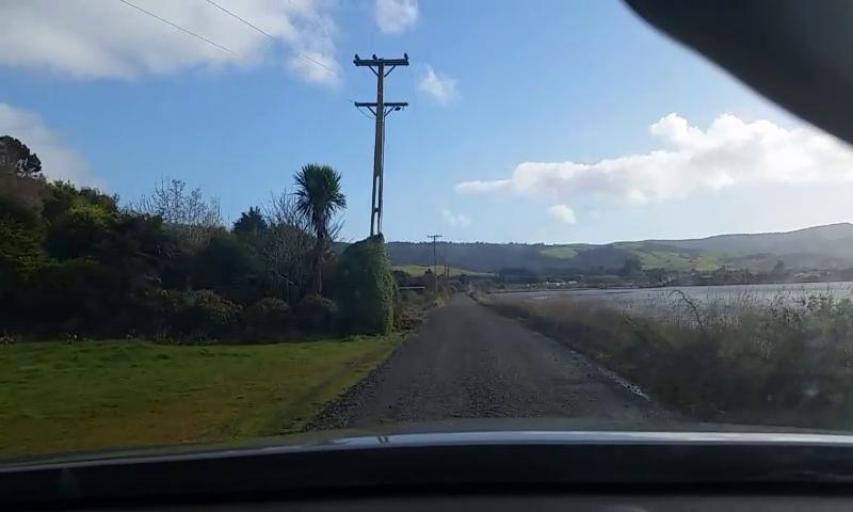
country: NZ
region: Otago
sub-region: Clutha District
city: Papatowai
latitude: -46.6300
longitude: 169.1405
